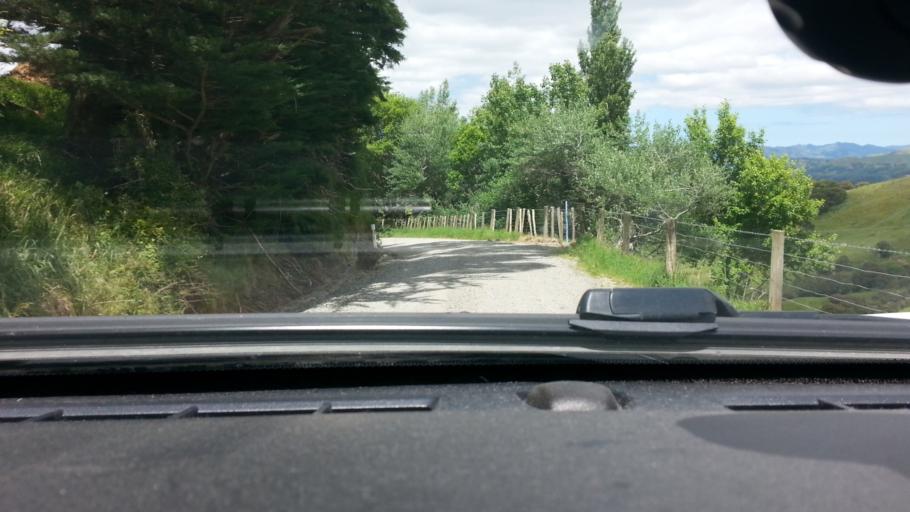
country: NZ
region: Wellington
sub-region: Masterton District
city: Masterton
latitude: -41.1602
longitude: 175.6824
